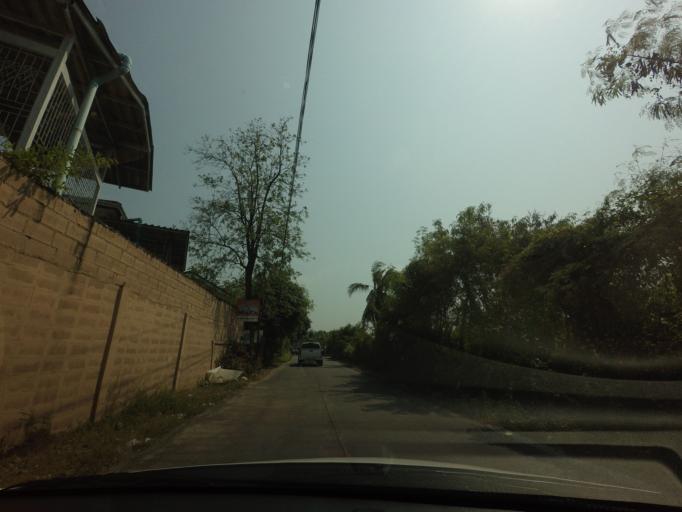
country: TH
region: Nakhon Pathom
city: Sam Phran
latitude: 13.7381
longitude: 100.2633
